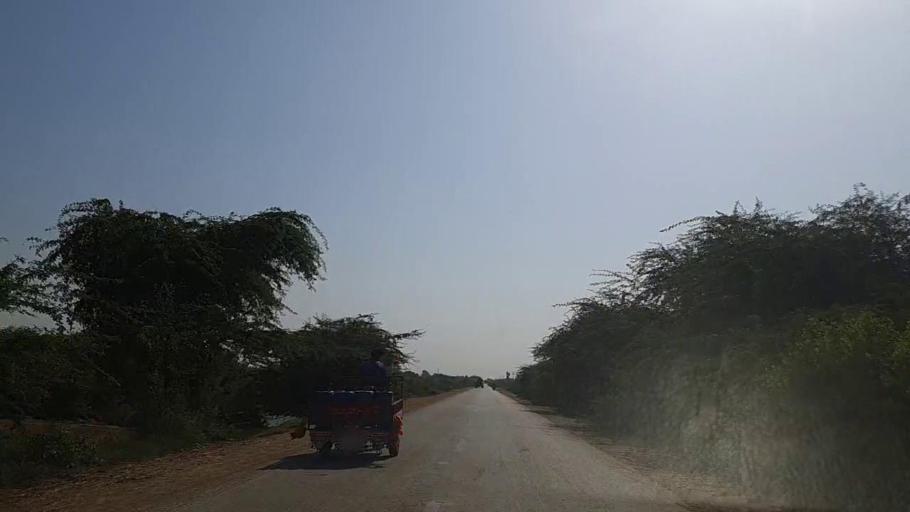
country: PK
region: Sindh
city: Mirpur Batoro
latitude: 24.6071
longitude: 68.2960
